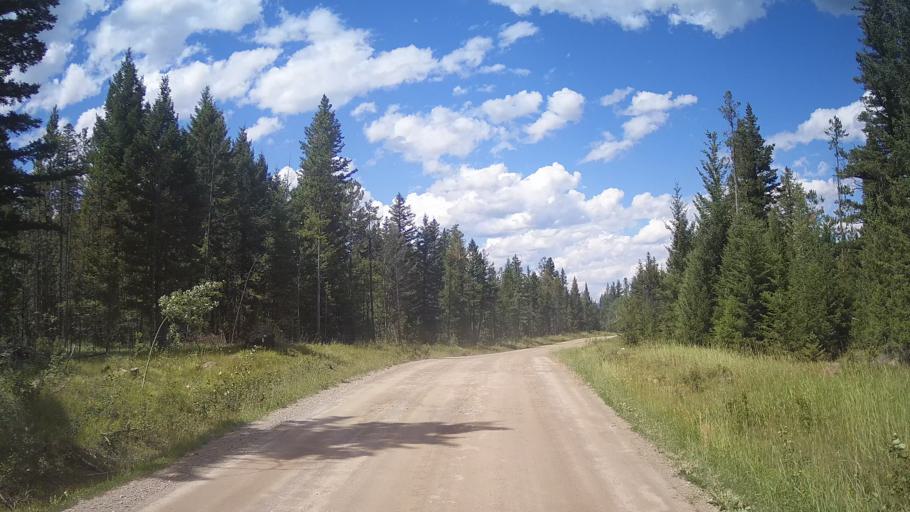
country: CA
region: British Columbia
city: Lillooet
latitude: 51.3178
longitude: -121.8609
